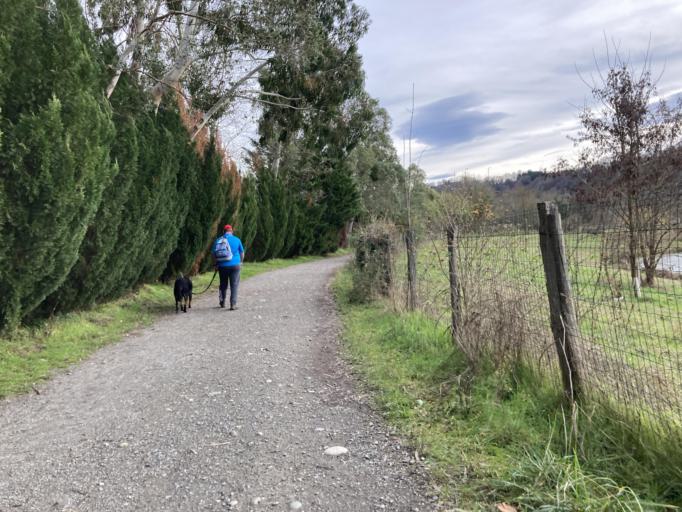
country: FR
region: Aquitaine
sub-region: Departement des Pyrenees-Atlantiques
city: Lescar
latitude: 43.3101
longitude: -0.4333
